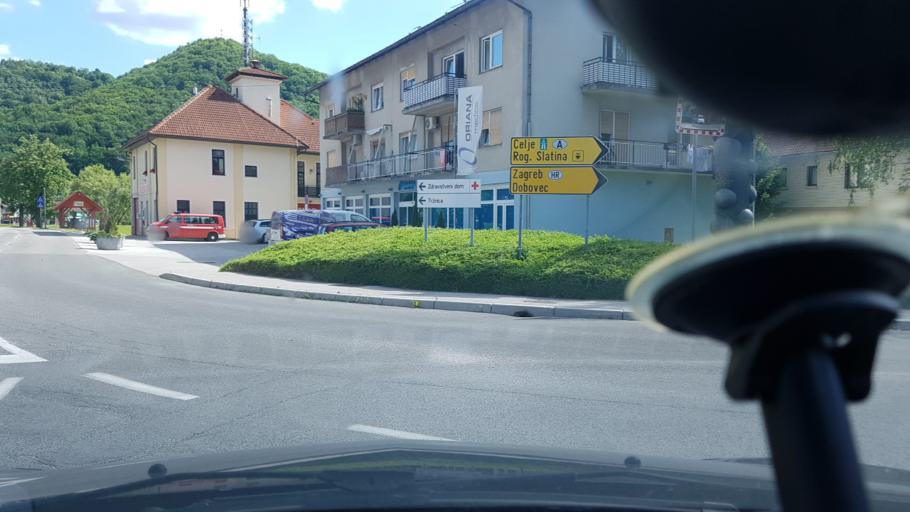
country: SI
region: Rogatec
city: Rogatec
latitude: 46.2259
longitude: 15.7000
